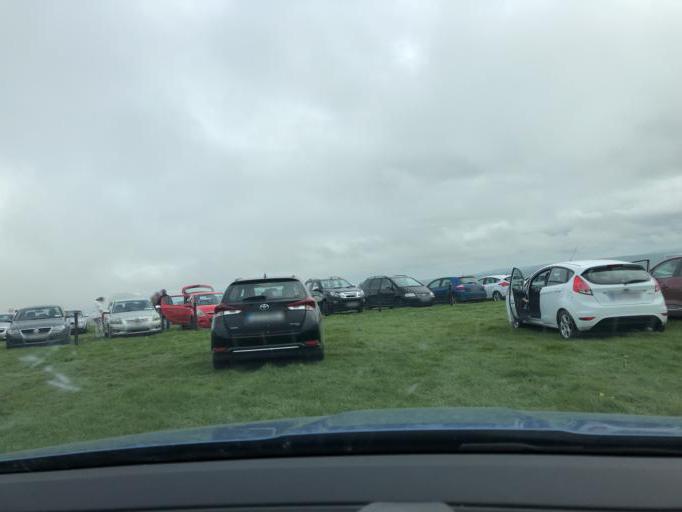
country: IE
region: Munster
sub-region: An Clar
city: Kilrush
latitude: 52.9645
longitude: -9.4351
